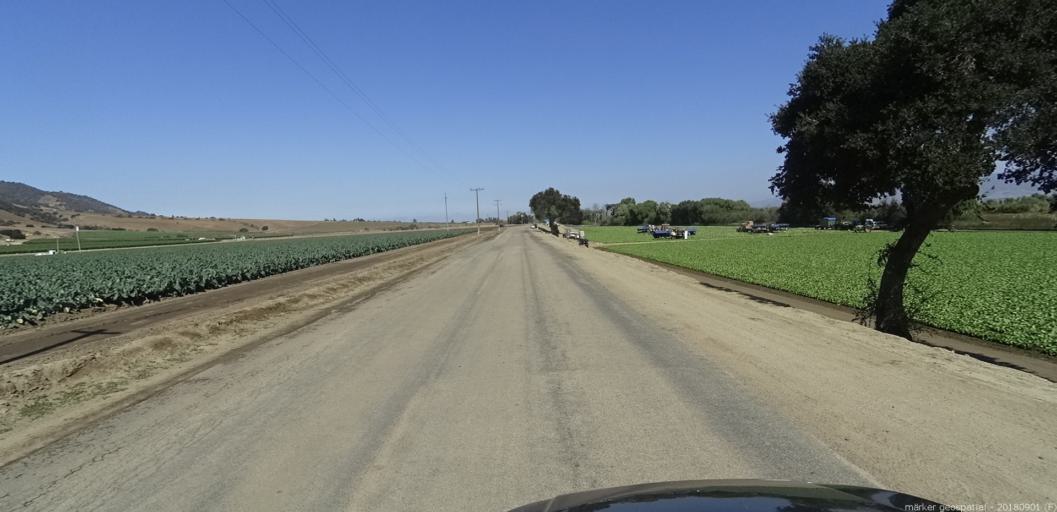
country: US
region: California
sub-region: Monterey County
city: Chualar
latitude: 36.5436
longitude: -121.5440
